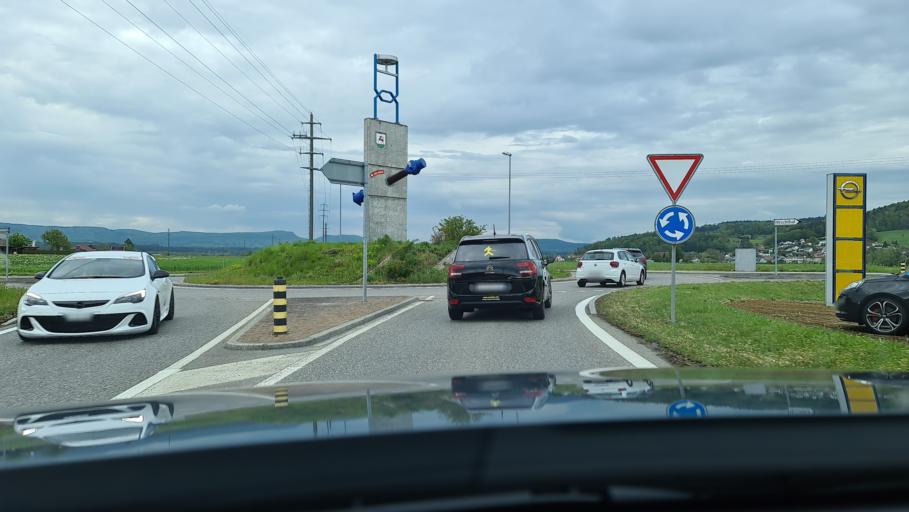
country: CH
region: Aargau
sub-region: Bezirk Kulm
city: Schoftland
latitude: 47.3195
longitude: 8.0471
